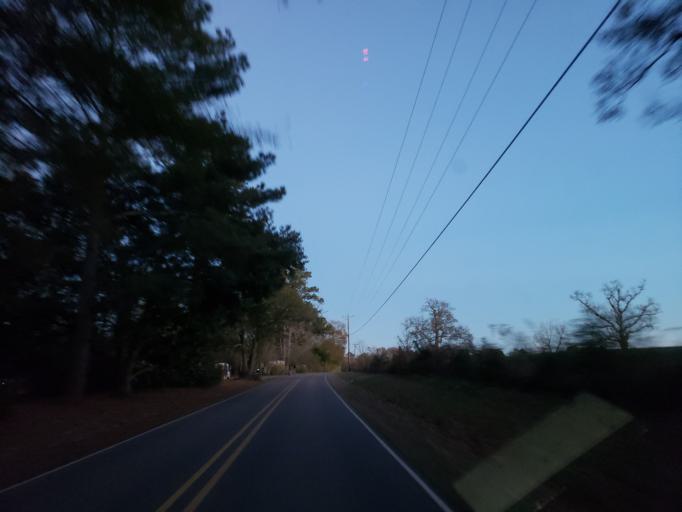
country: US
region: Mississippi
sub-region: Forrest County
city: Rawls Springs
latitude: 31.4245
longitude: -89.3513
